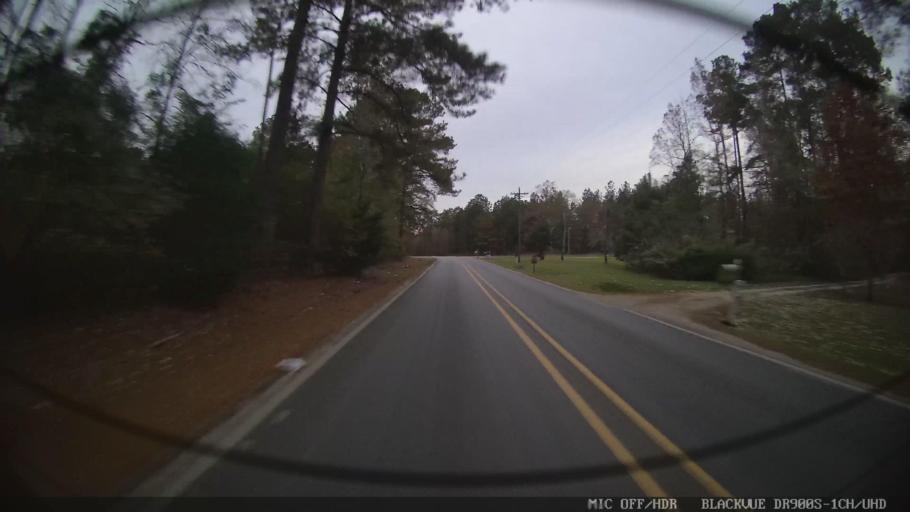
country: US
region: Mississippi
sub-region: Clarke County
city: Quitman
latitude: 32.0294
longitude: -88.8201
